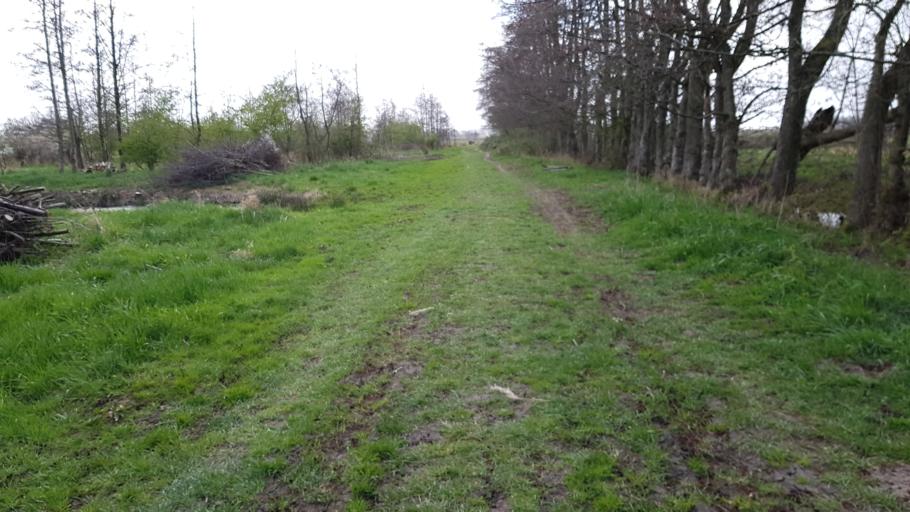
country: NL
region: Utrecht
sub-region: Gemeente Lopik
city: Lopik
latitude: 51.9531
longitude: 4.9966
